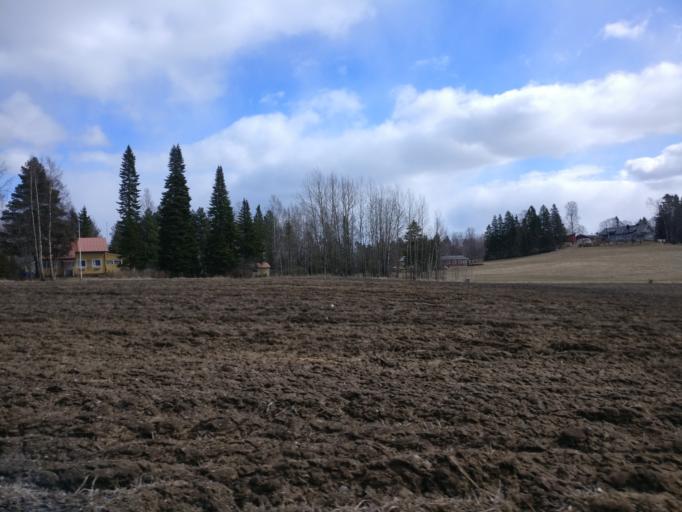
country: FI
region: Uusimaa
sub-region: Helsinki
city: Karjalohja
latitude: 60.2471
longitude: 23.7374
